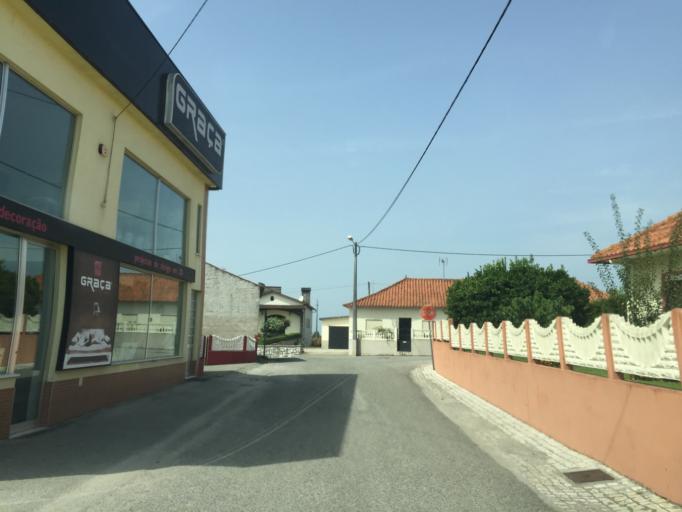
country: PT
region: Leiria
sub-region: Leiria
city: Monte Redondo
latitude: 39.9457
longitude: -8.7880
